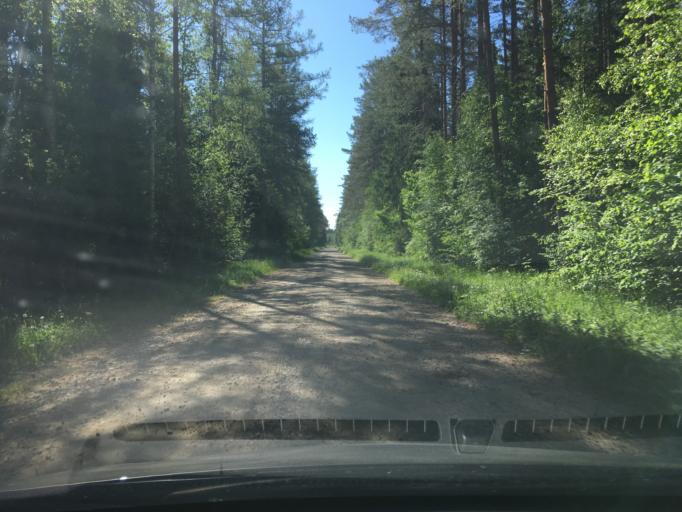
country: EE
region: Laeaene
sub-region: Lihula vald
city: Lihula
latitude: 58.6372
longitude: 23.7942
